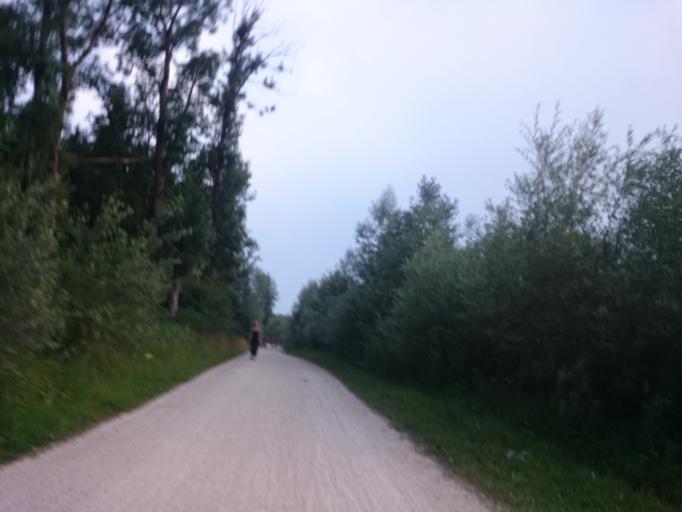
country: DE
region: Bavaria
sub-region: Swabia
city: Stadtbergen
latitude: 48.3300
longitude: 10.8511
